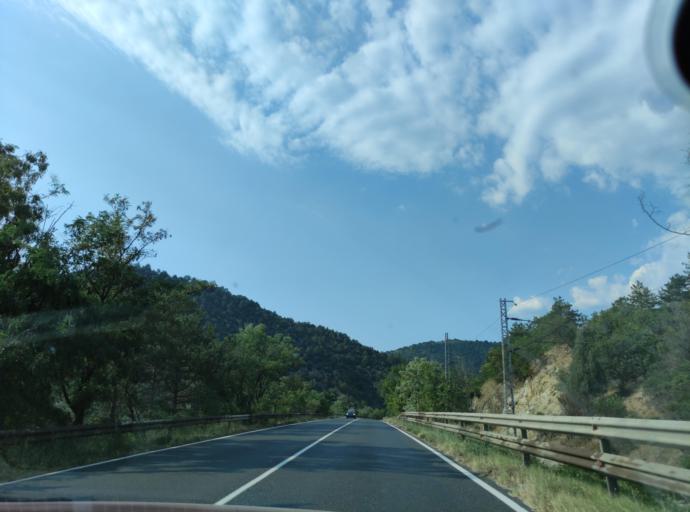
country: BG
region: Blagoevgrad
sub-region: Obshtina Kresna
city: Kresna
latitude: 41.7385
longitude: 23.1590
